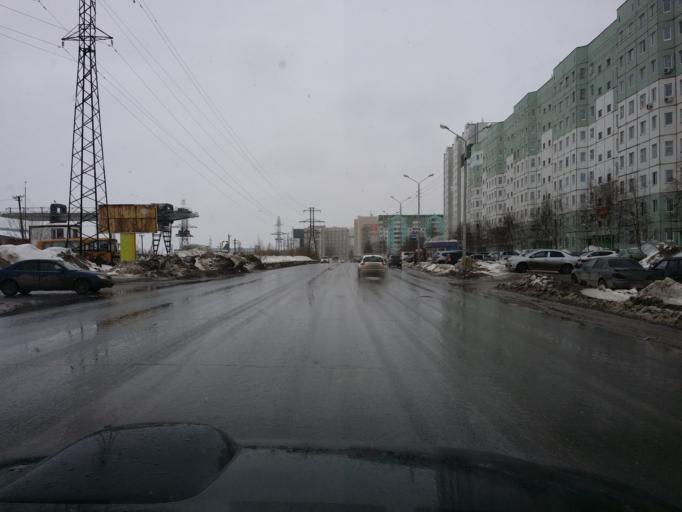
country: RU
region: Khanty-Mansiyskiy Avtonomnyy Okrug
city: Nizhnevartovsk
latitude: 60.9558
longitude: 76.5854
